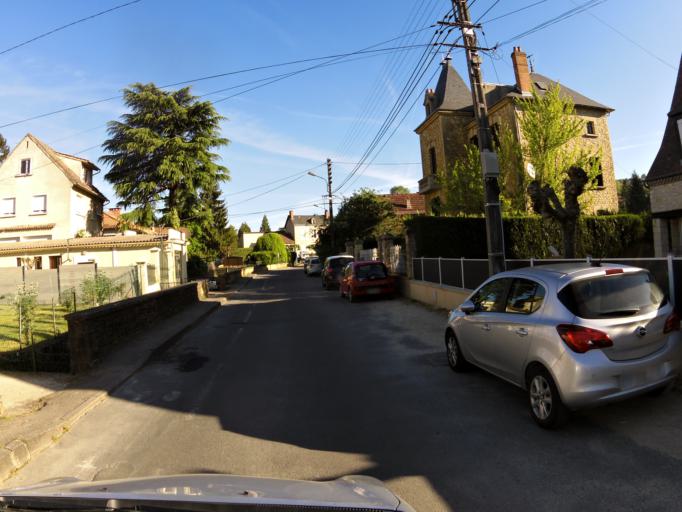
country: FR
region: Aquitaine
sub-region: Departement de la Dordogne
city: Sarlat-la-Caneda
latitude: 44.8966
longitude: 1.2147
